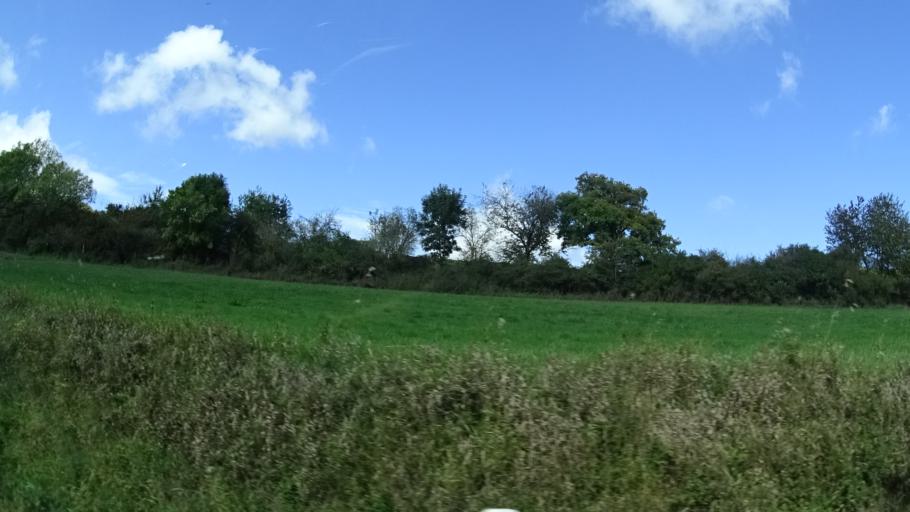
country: DE
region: Bavaria
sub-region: Regierungsbezirk Unterfranken
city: Buchbrunn
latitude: 49.7356
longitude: 10.1081
